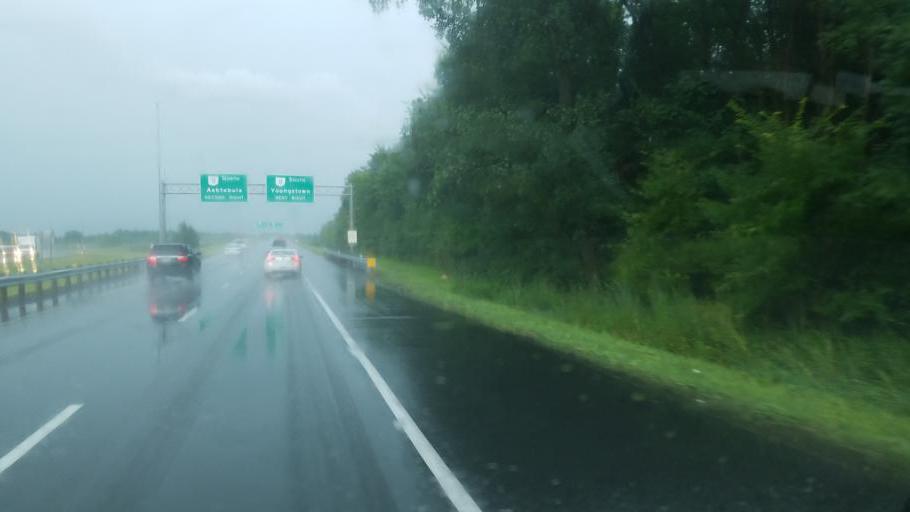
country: US
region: Ohio
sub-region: Trumbull County
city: Howland Center
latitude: 41.2283
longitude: -80.7193
